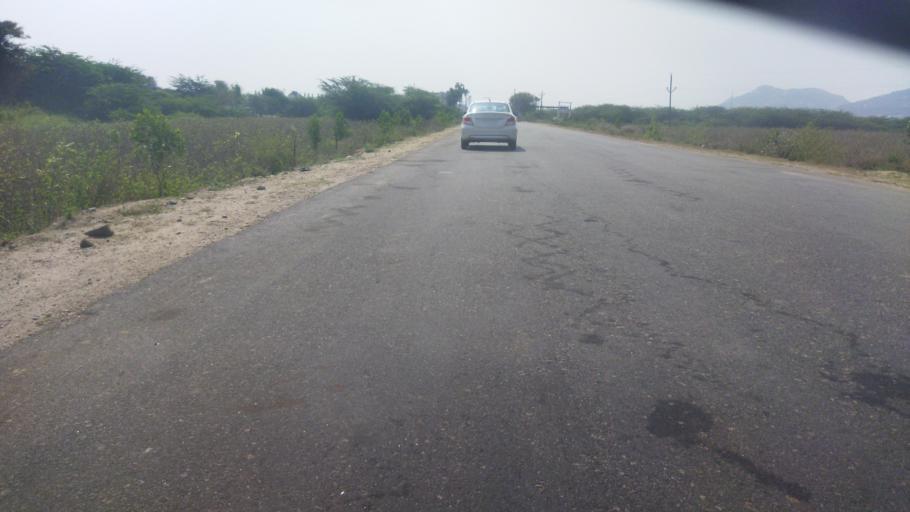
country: IN
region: Telangana
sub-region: Nalgonda
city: Nalgonda
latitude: 17.0814
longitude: 79.2839
